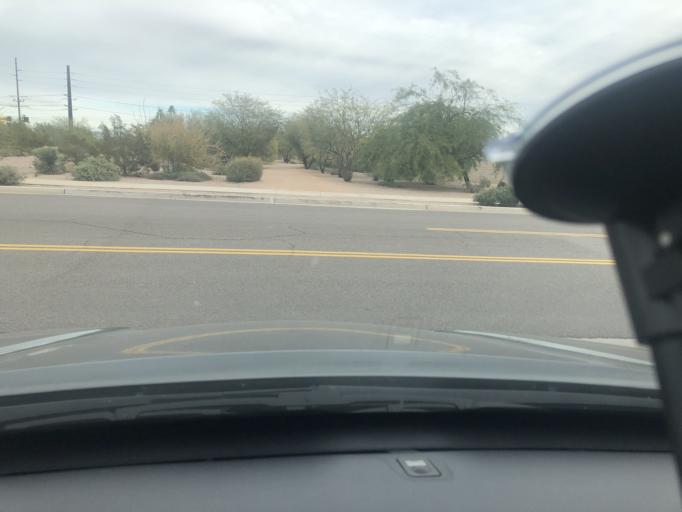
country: US
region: Arizona
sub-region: Maricopa County
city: Scottsdale
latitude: 33.5235
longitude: -111.9175
